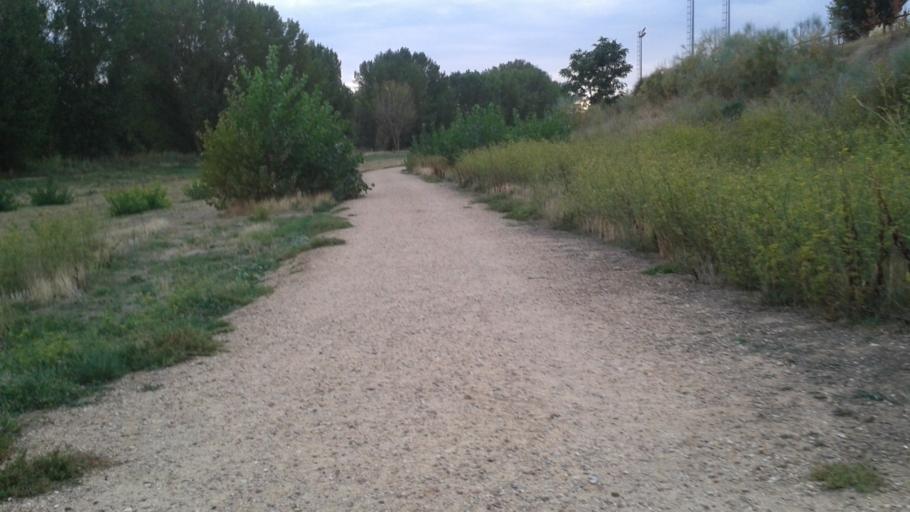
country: ES
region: Castille and Leon
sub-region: Provincia de Valladolid
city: Arroyo
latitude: 41.6116
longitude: -4.7807
